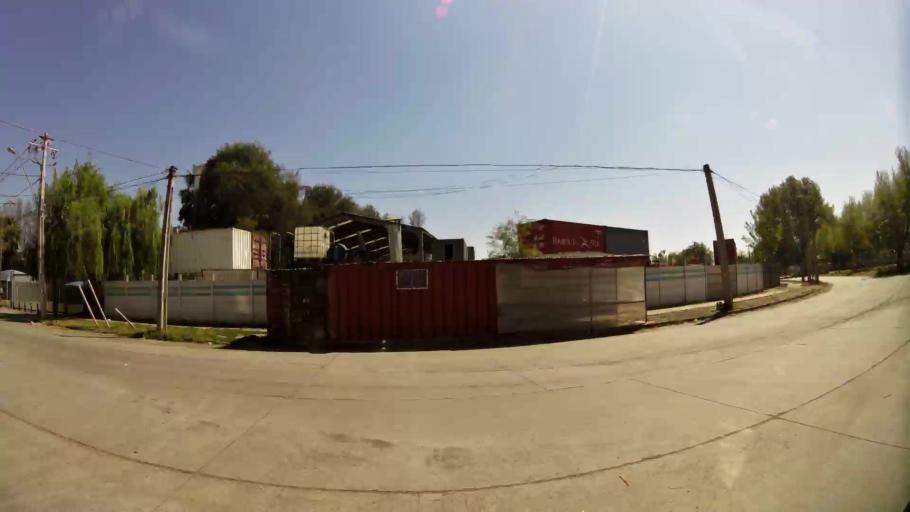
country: CL
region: Santiago Metropolitan
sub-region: Provincia de Santiago
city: Lo Prado
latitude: -33.3802
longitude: -70.7437
